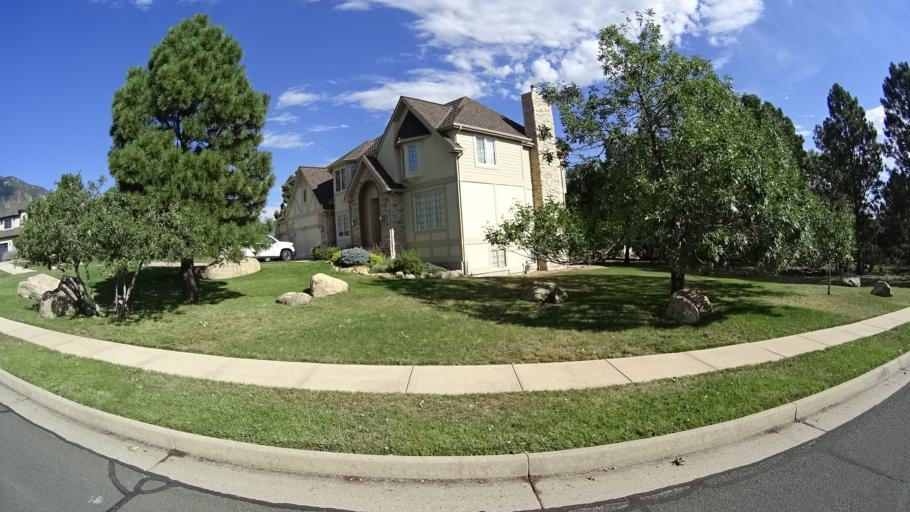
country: US
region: Colorado
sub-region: El Paso County
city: Stratmoor
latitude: 38.7672
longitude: -104.8298
